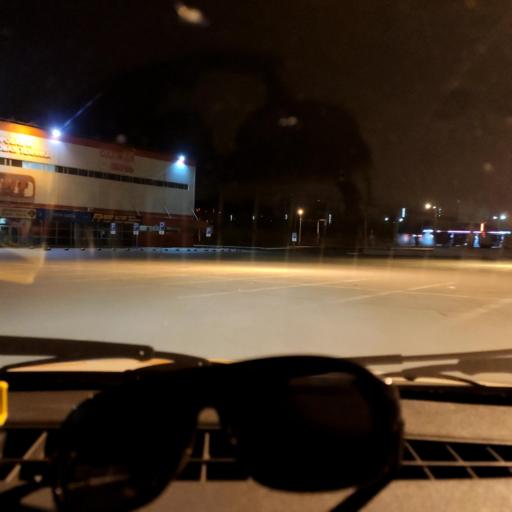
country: RU
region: Bashkortostan
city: Mikhaylovka
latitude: 54.7056
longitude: 55.8453
